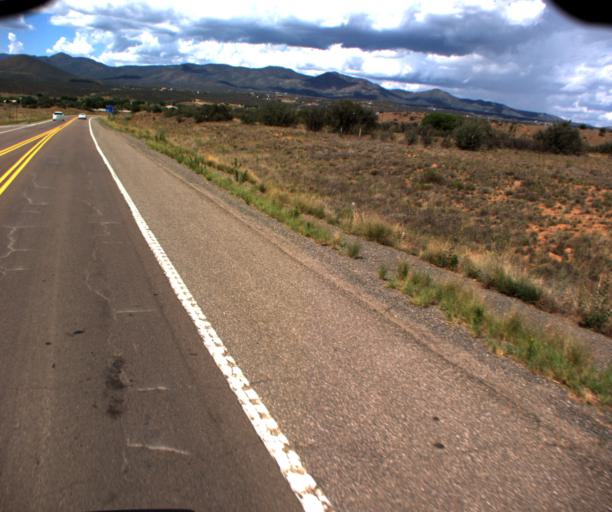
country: US
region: Arizona
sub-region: Yavapai County
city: Dewey-Humboldt
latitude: 34.5313
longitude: -112.2208
